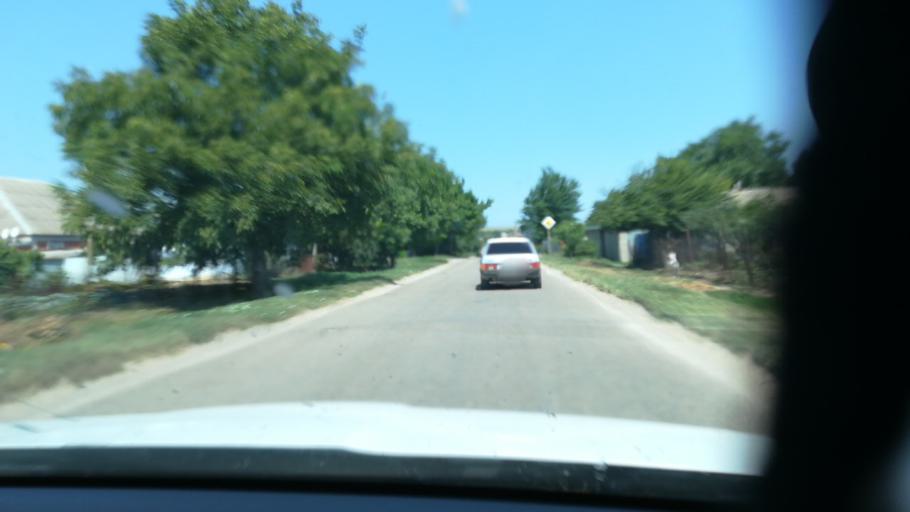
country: RU
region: Krasnodarskiy
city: Starotitarovskaya
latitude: 45.2081
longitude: 37.1460
